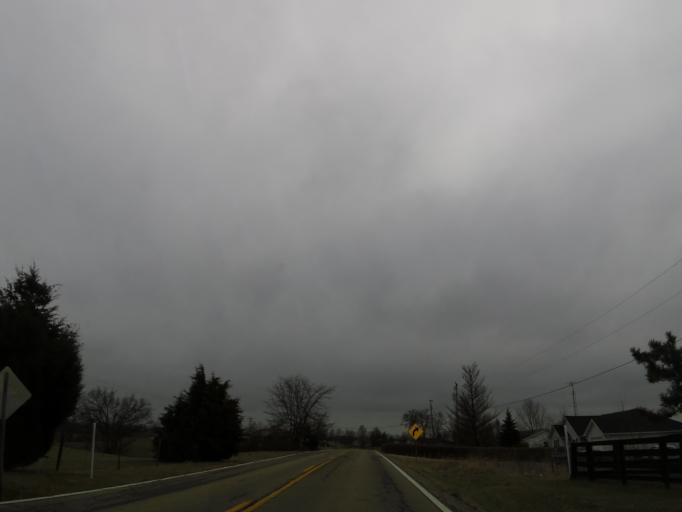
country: US
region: Kentucky
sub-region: Trimble County
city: Providence
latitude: 38.5340
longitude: -85.2568
